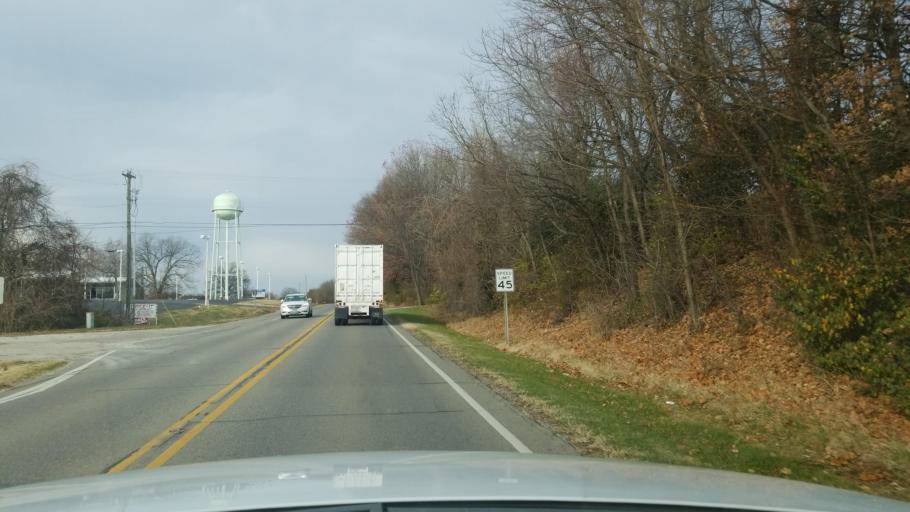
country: US
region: Indiana
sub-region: Posey County
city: Mount Vernon
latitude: 37.9282
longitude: -87.9184
